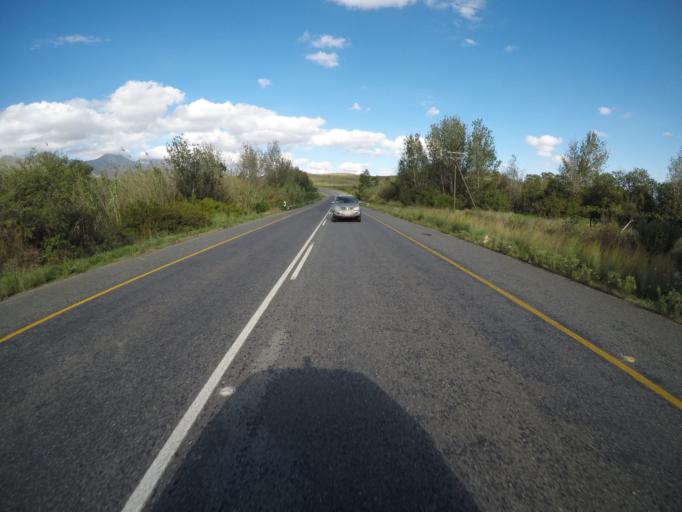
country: ZA
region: Western Cape
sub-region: Cape Winelands District Municipality
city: Ashton
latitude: -33.9484
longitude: 20.2187
